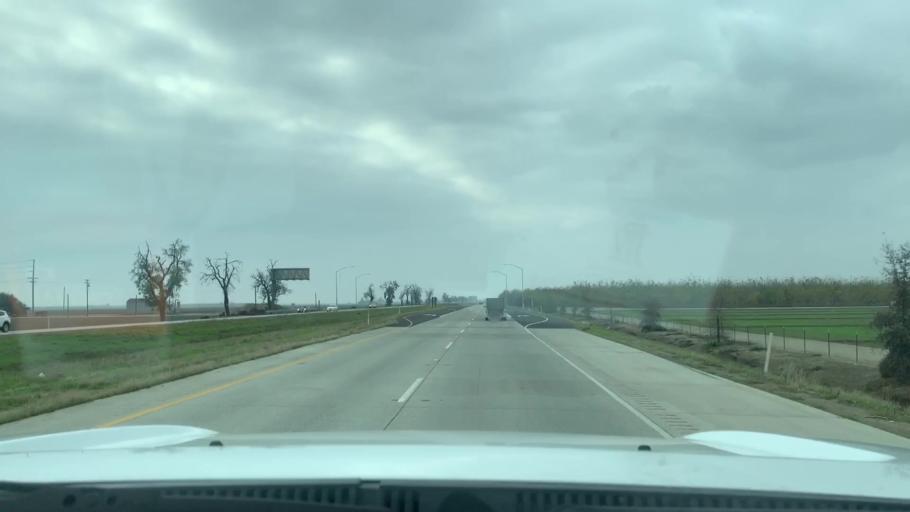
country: US
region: California
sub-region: Tulare County
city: Goshen
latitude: 36.3277
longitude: -119.4459
